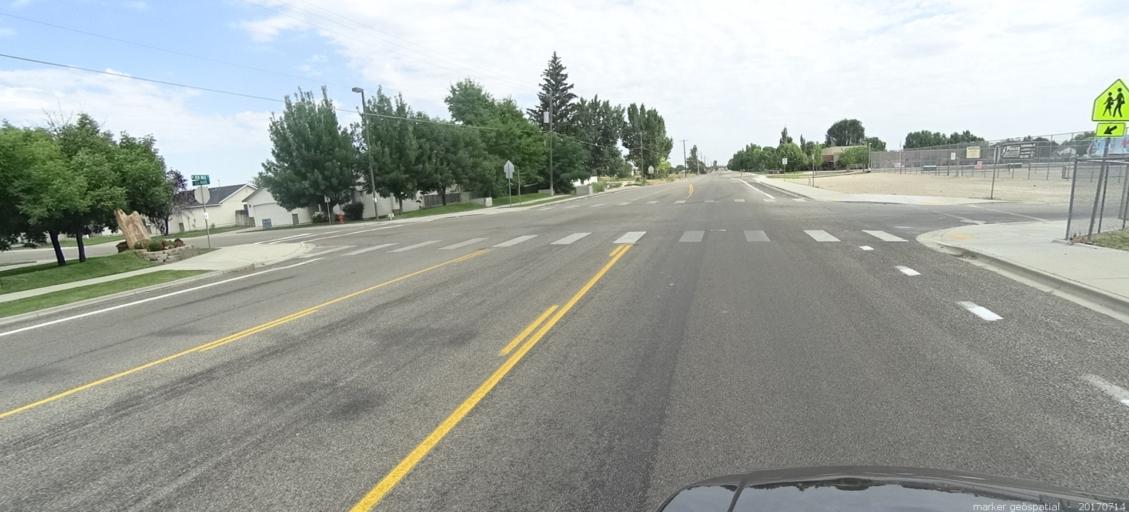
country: US
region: Idaho
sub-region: Ada County
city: Kuna
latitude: 43.4968
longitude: -116.4335
